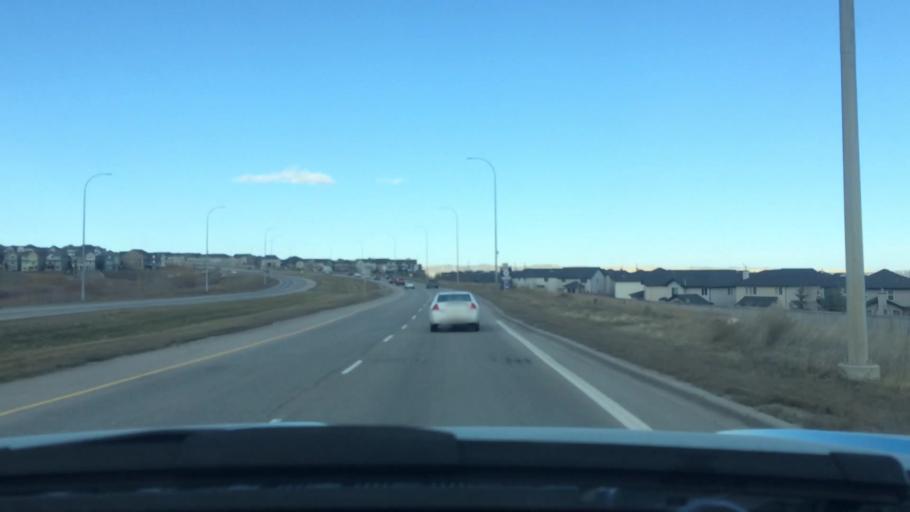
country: CA
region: Alberta
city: Calgary
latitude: 51.1577
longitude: -114.1409
